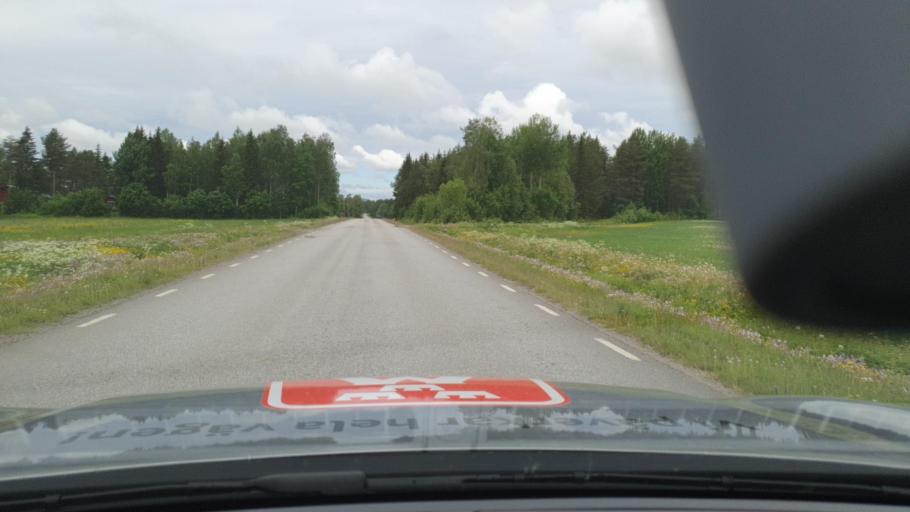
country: SE
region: Norrbotten
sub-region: Lulea Kommun
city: Ranea
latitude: 65.9537
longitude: 22.1189
